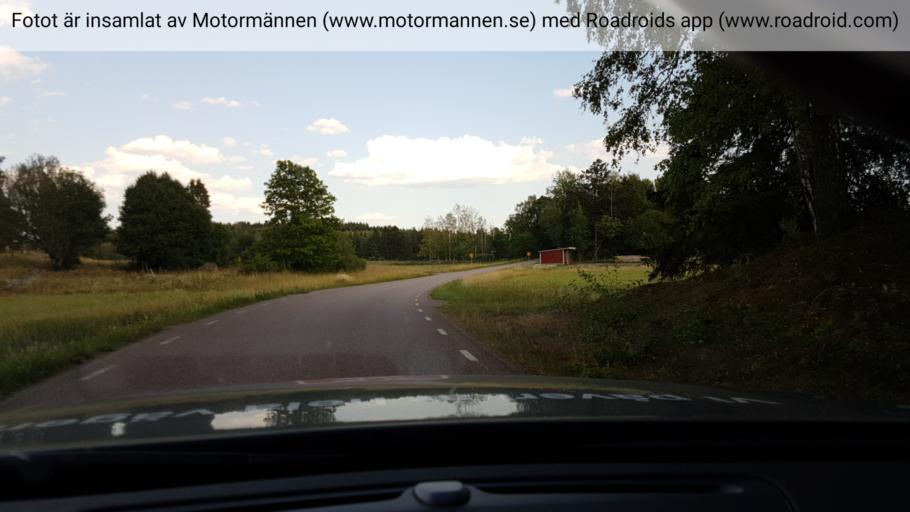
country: SE
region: Vaestmanland
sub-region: Vasteras
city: Tillberga
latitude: 59.6825
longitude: 16.6975
